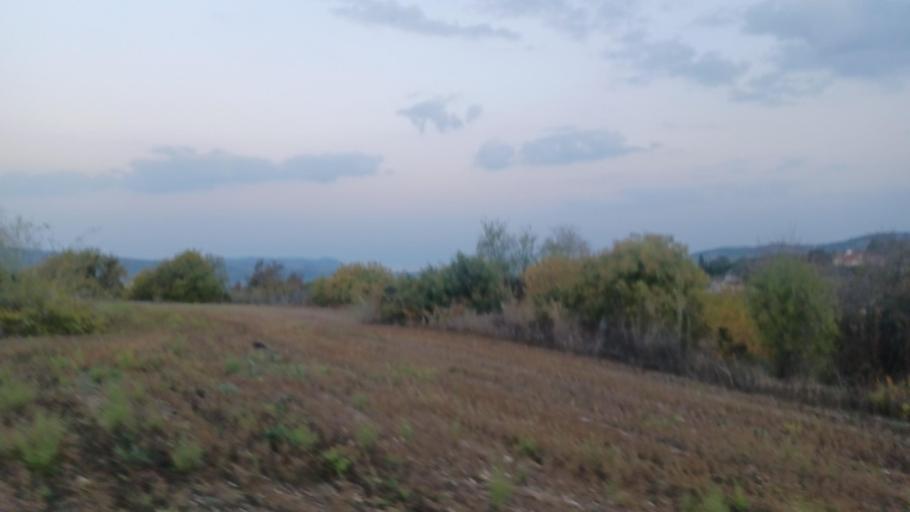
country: CY
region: Pafos
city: Tala
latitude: 34.9342
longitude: 32.5104
